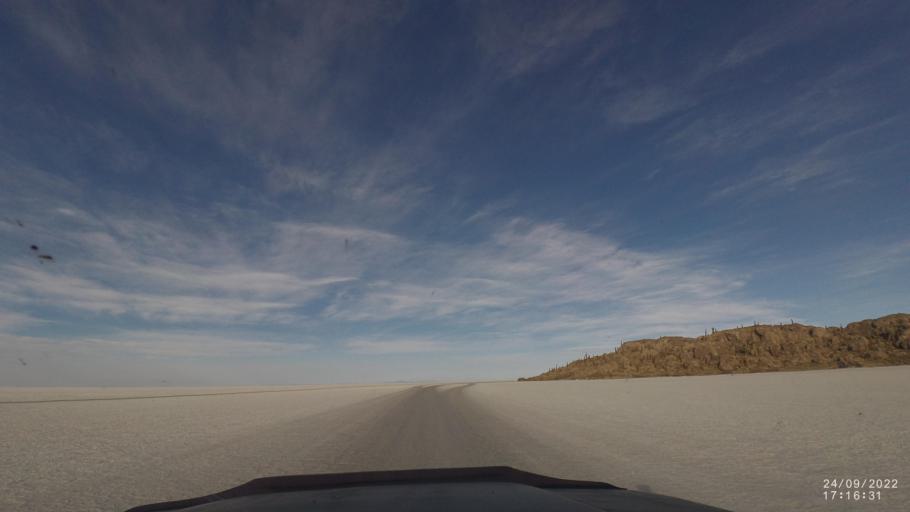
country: BO
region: Potosi
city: Colchani
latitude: -20.2394
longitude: -67.6257
